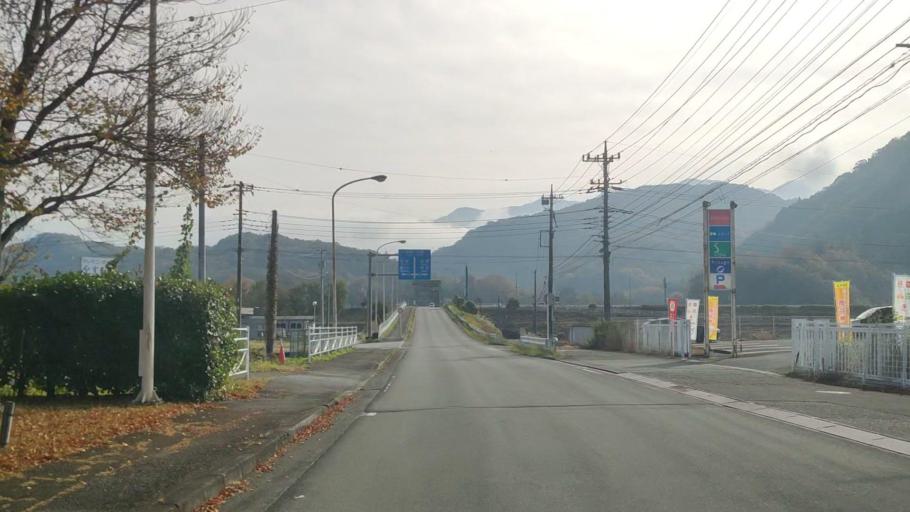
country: JP
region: Yamanashi
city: Ryuo
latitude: 35.4865
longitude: 138.4504
